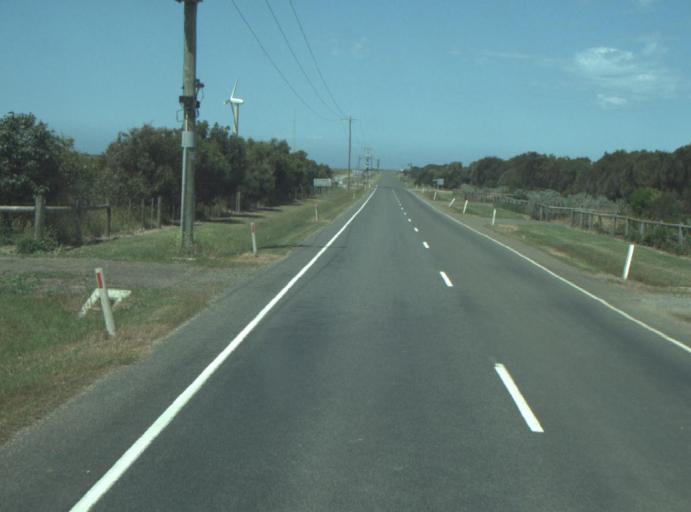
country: AU
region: Victoria
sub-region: Greater Geelong
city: Leopold
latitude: -38.2764
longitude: 144.4212
